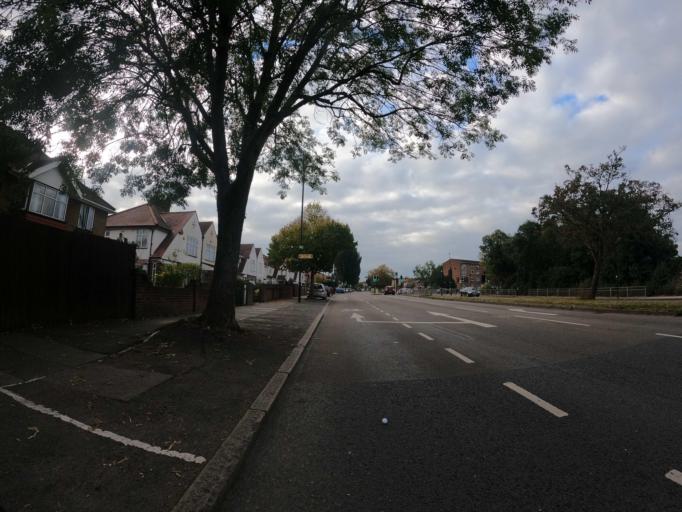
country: GB
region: England
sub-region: Greater London
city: Southall
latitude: 51.5105
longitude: -0.3629
